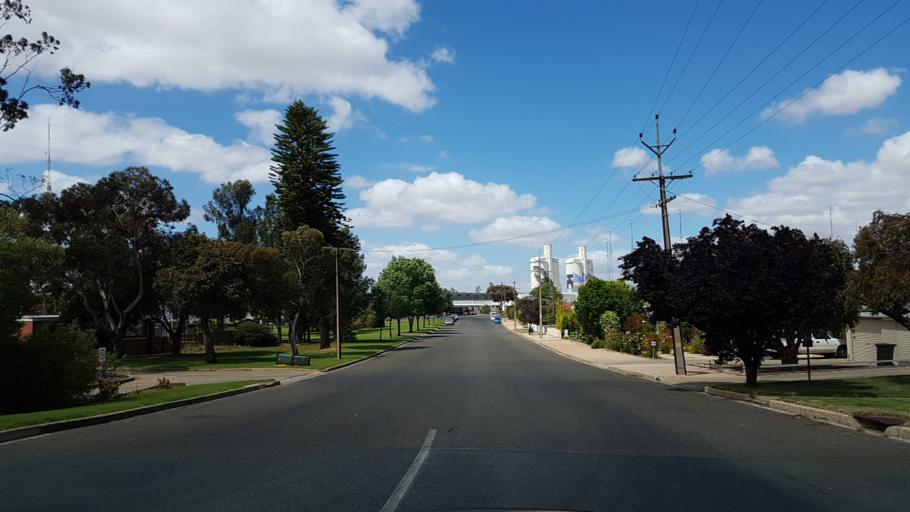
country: AU
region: South Australia
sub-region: Loxton Waikerie
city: Waikerie
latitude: -34.1829
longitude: 139.9865
